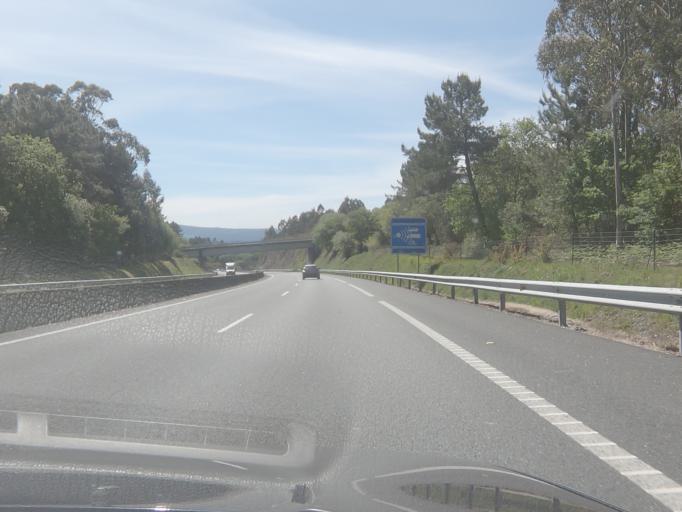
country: ES
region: Galicia
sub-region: Provincia da Coruna
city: Santiago de Compostela
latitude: 42.8086
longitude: -8.6007
